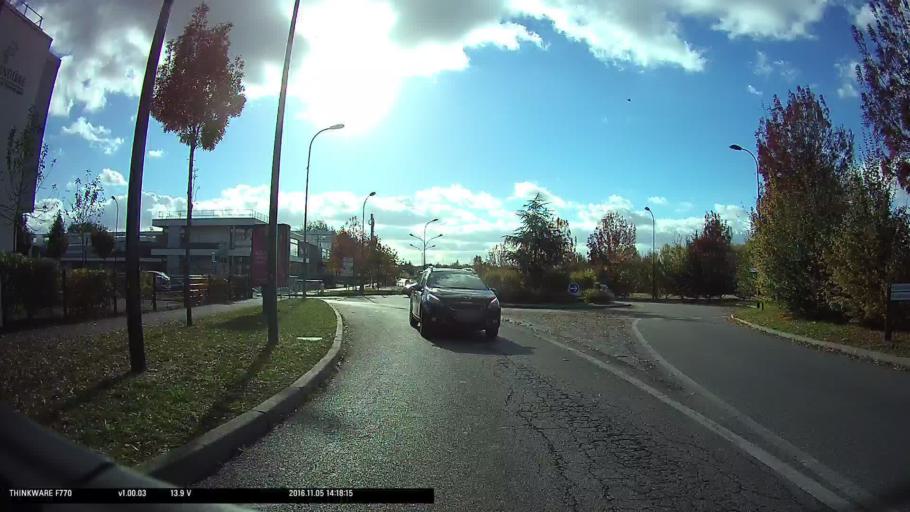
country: FR
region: Ile-de-France
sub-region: Departement du Val-d'Oise
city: Osny
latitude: 49.0751
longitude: 2.0729
